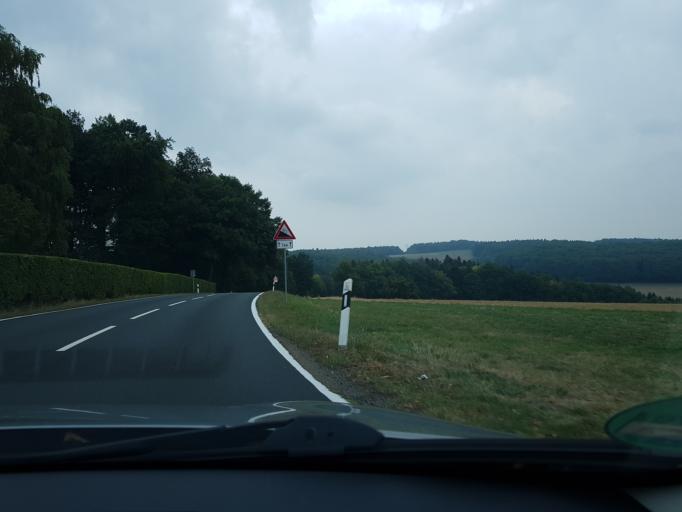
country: DE
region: Rheinland-Pfalz
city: Becheln
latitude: 50.2899
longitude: 7.7235
